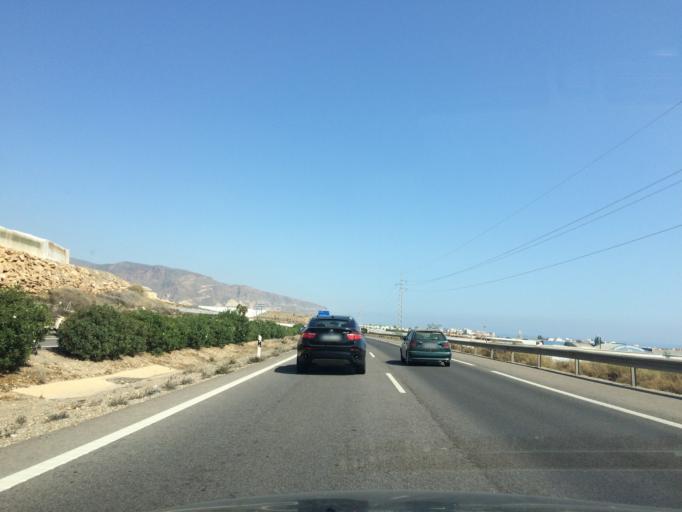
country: ES
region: Andalusia
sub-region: Provincia de Almeria
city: Vicar
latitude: 36.8124
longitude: -2.6151
